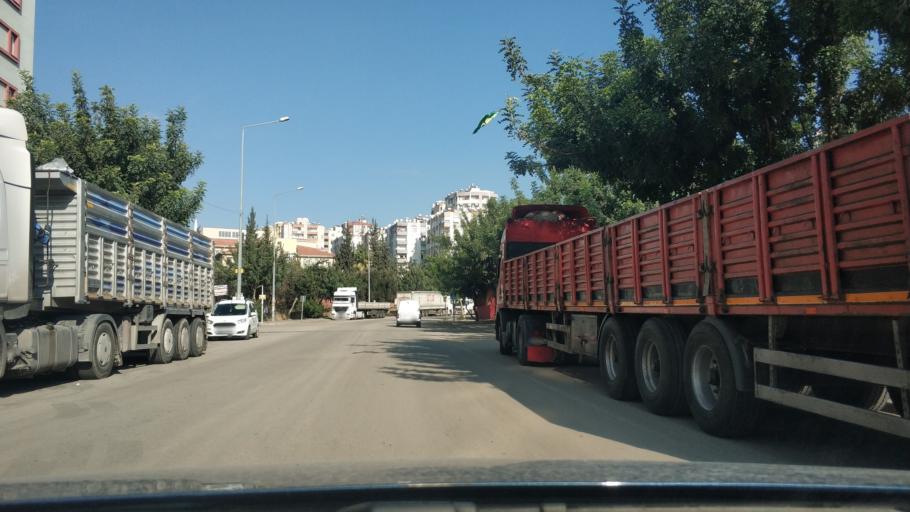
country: TR
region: Adana
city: Seyhan
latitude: 37.0212
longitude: 35.2911
